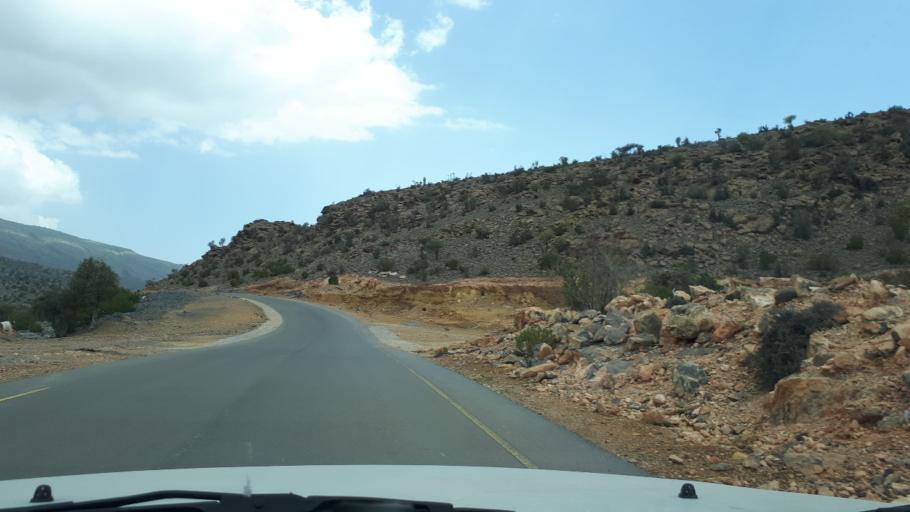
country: OM
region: Muhafazat ad Dakhiliyah
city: Bahla'
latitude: 23.2249
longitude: 57.2028
